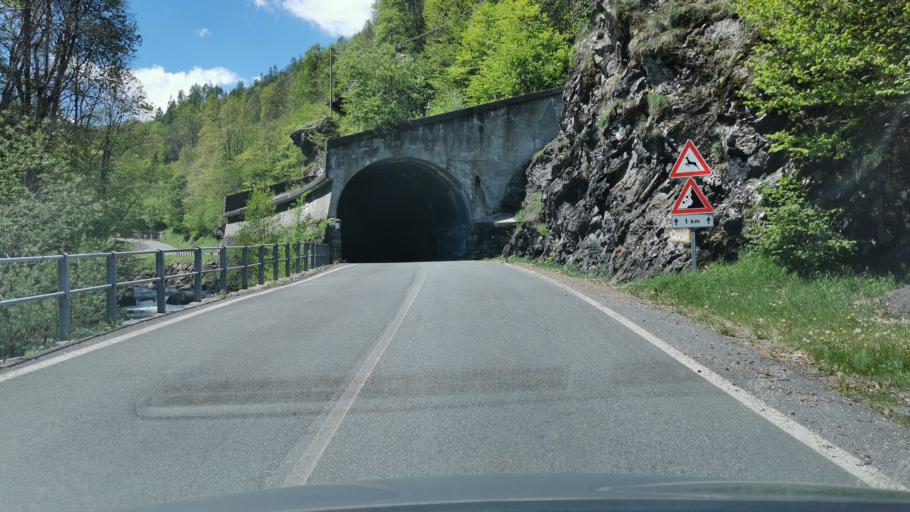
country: IT
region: Piedmont
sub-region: Provincia di Torino
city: Usseglio
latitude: 45.2294
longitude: 7.2023
